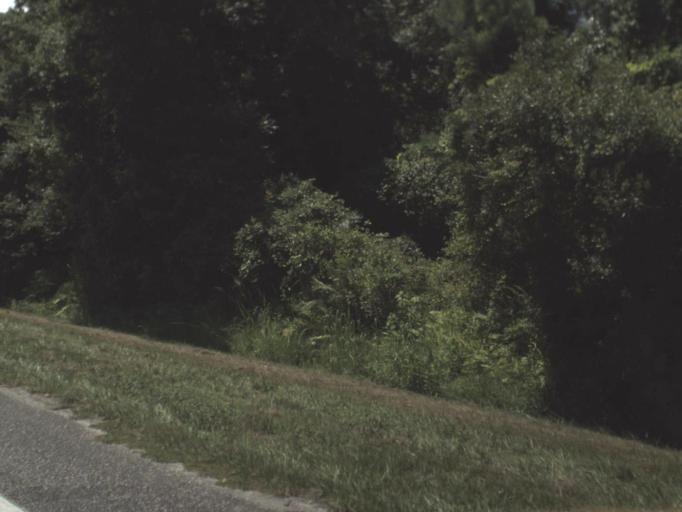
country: US
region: Florida
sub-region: Putnam County
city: Crescent City
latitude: 29.4776
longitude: -81.5418
